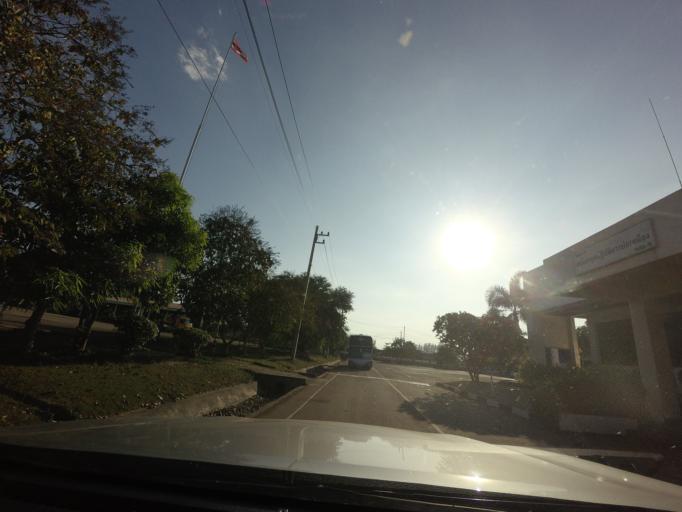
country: TH
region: Lampang
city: Mae Mo
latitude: 18.3090
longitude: 99.7394
